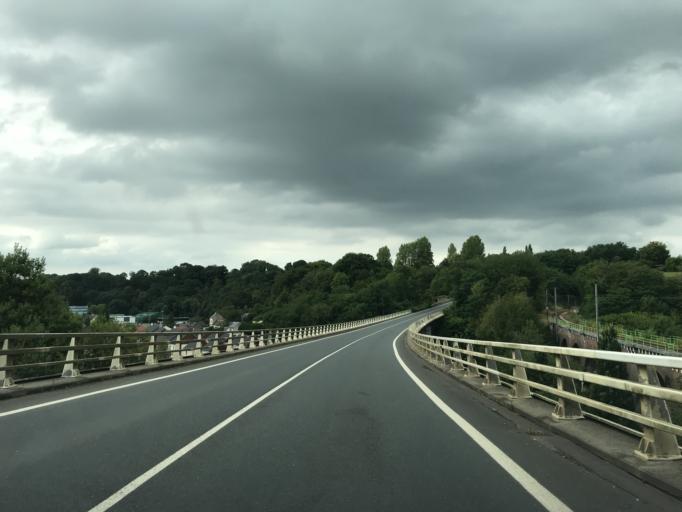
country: FR
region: Haute-Normandie
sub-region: Departement de la Seine-Maritime
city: Bolbec
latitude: 49.5638
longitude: 0.4680
